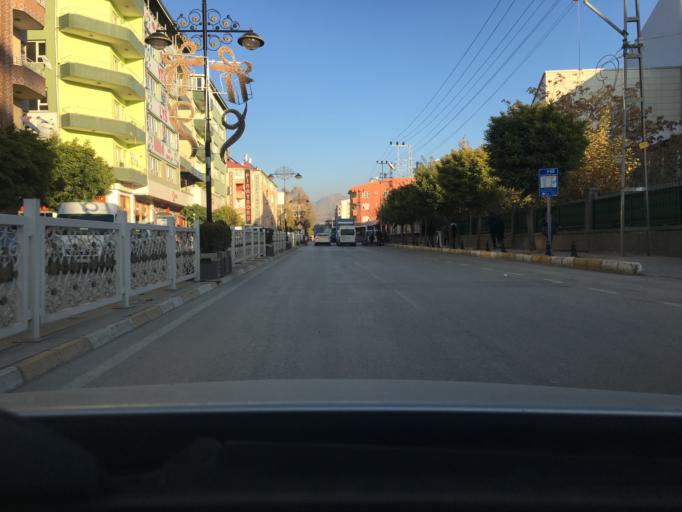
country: TR
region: Van
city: Van
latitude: 38.4981
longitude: 43.3979
